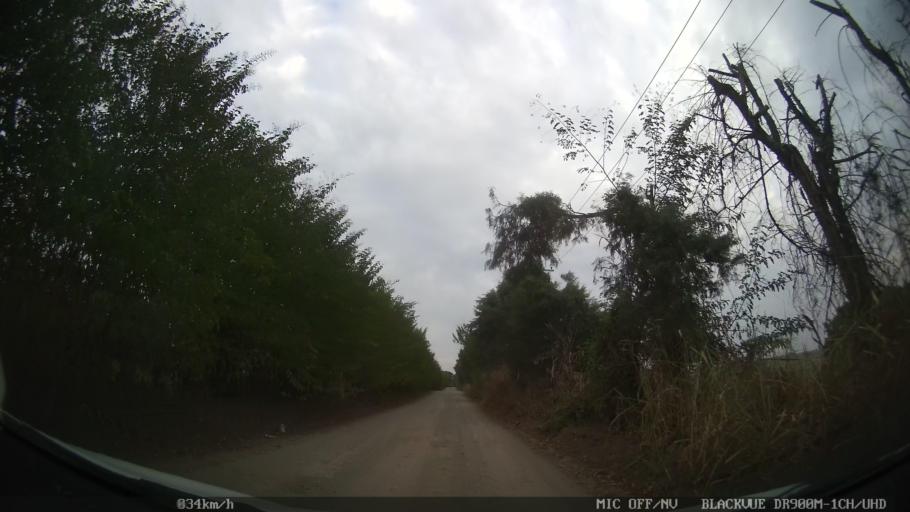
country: BR
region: Sao Paulo
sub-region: Americana
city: Americana
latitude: -22.6695
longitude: -47.3745
